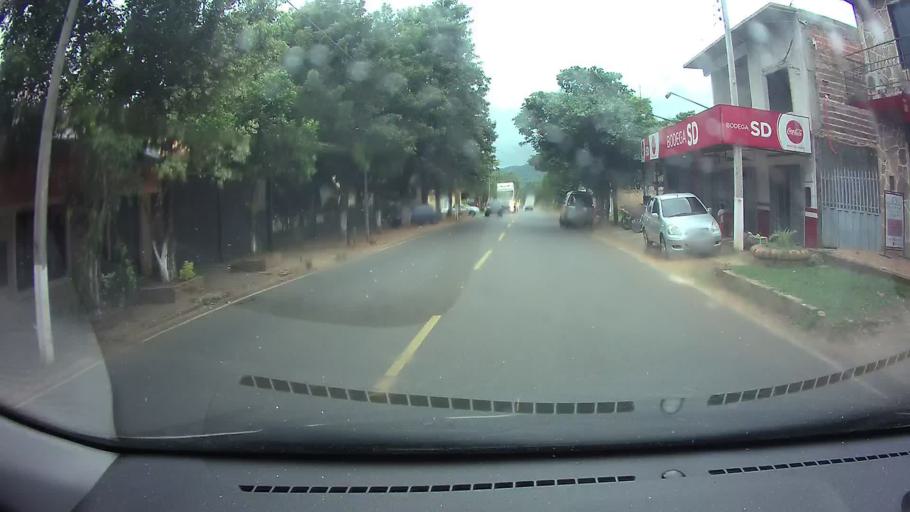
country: PY
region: Paraguari
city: Carapegua
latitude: -25.7656
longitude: -57.2481
